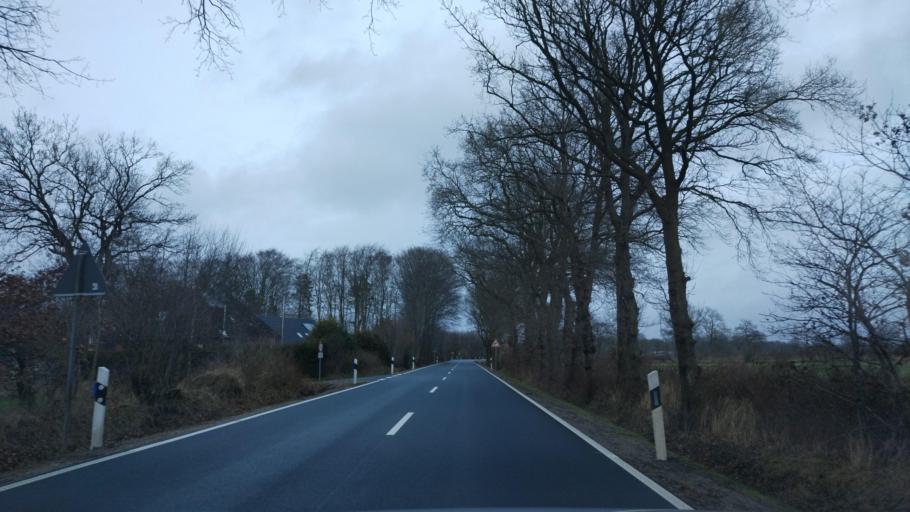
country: DE
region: Schleswig-Holstein
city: Klein Bennebek
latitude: 54.4003
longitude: 9.4599
